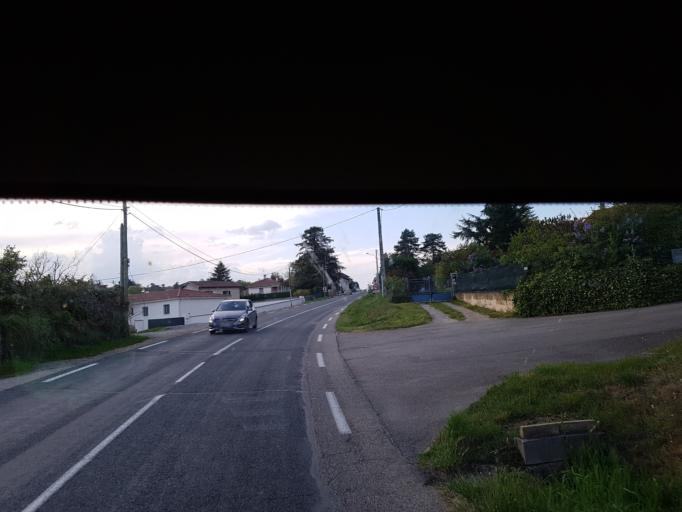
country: FR
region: Rhone-Alpes
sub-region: Departement du Rhone
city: Sainte-Consorce
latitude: 45.7930
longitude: 4.6902
